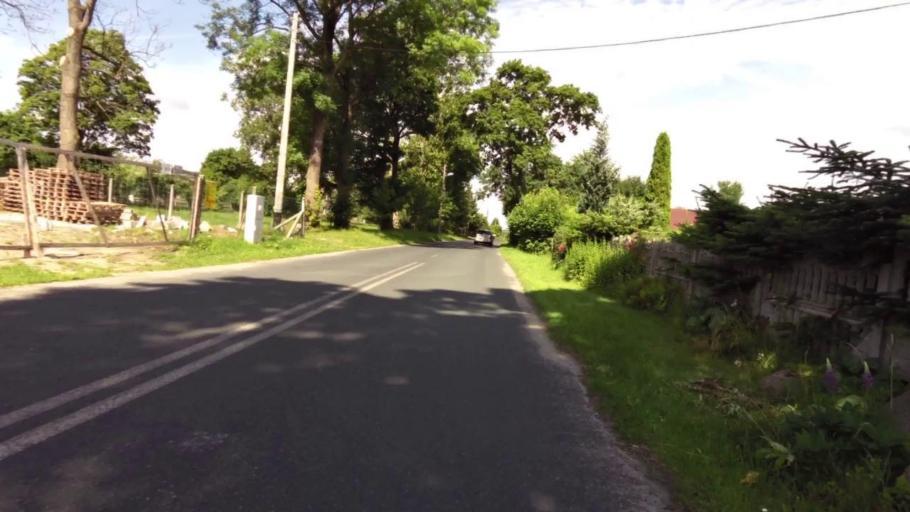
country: PL
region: West Pomeranian Voivodeship
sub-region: Powiat stargardzki
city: Dobrzany
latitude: 53.4124
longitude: 15.4211
